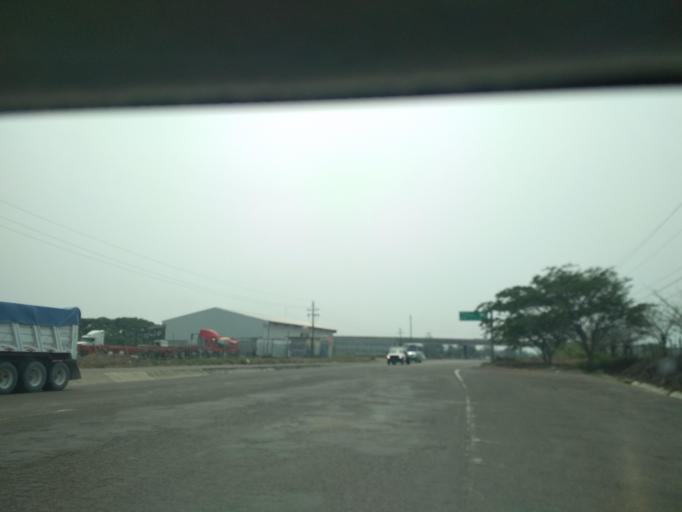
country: MX
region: Veracruz
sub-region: Veracruz
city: Delfino Victoria (Santa Fe)
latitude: 19.1879
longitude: -96.2718
